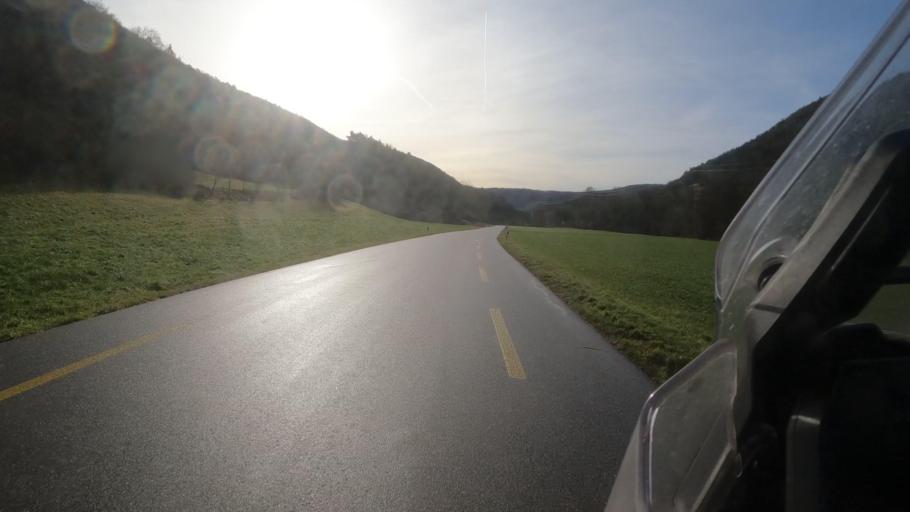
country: CH
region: Schaffhausen
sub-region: Bezirk Reiat
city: Stetten
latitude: 47.7775
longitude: 8.6184
